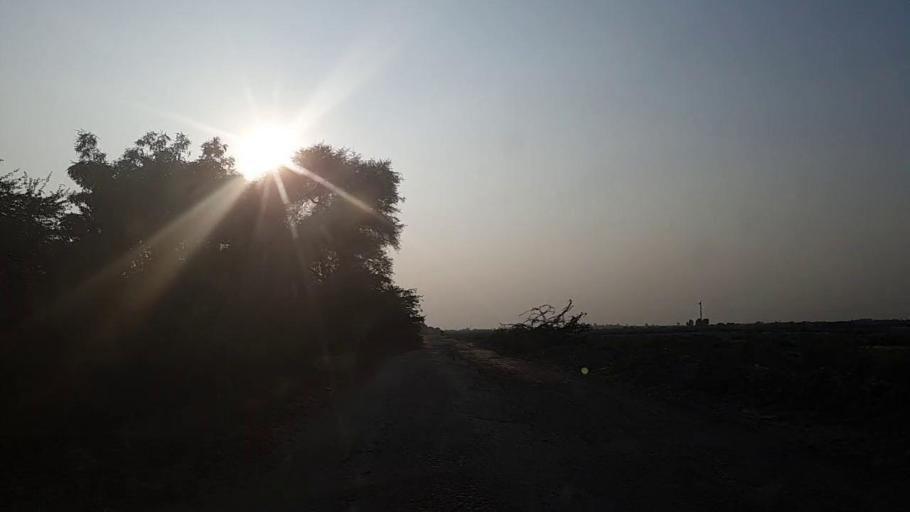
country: PK
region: Sindh
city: Mirpur Sakro
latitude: 24.5620
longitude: 67.6117
